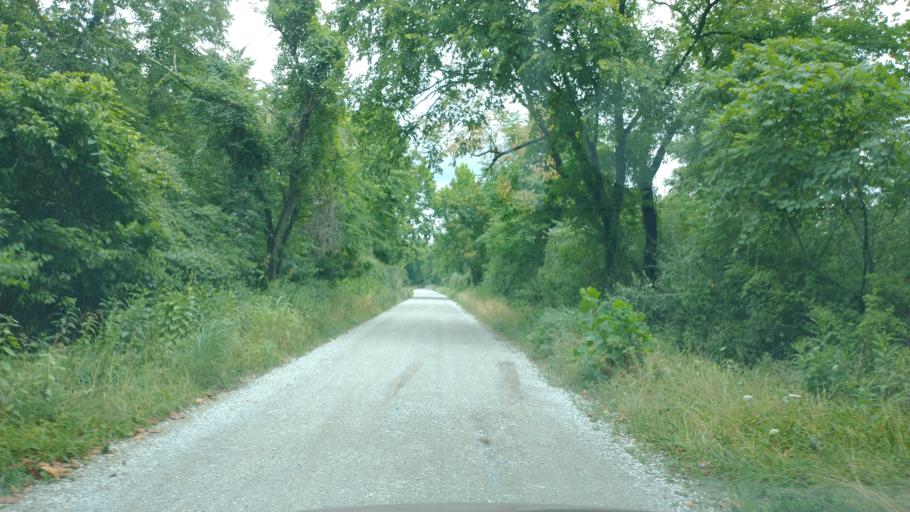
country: US
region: Ohio
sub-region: Meigs County
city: Middleport
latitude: 38.9272
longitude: -82.0696
